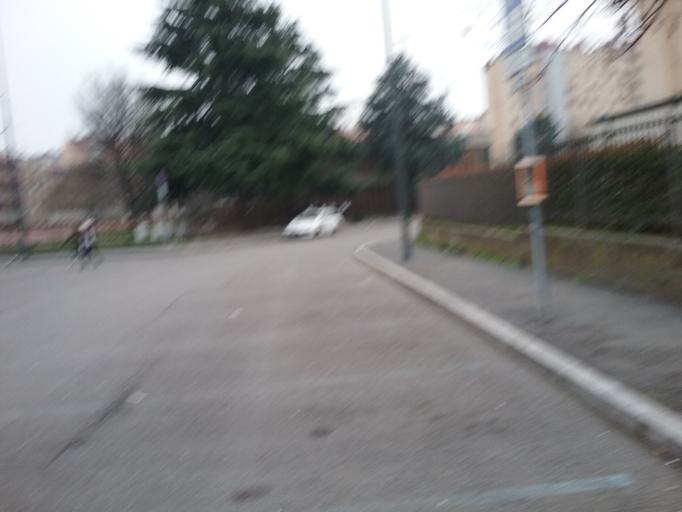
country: IT
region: Lombardy
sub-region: Citta metropolitana di Milano
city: Cesano Boscone
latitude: 45.4741
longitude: 9.1130
